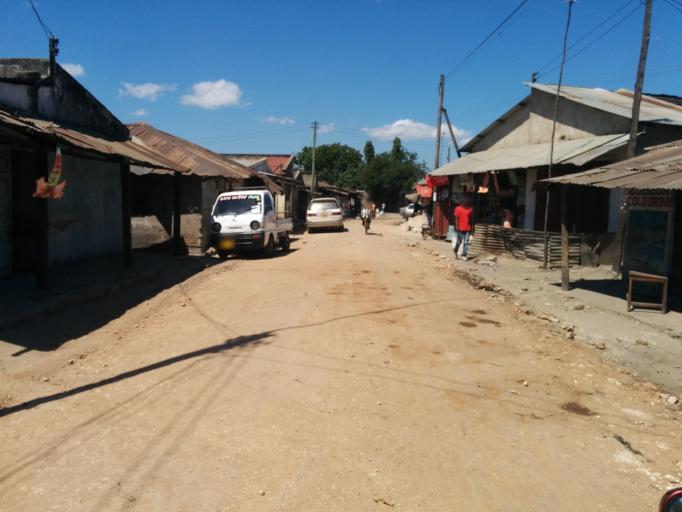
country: TZ
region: Dar es Salaam
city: Magomeni
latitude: -6.7959
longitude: 39.2462
